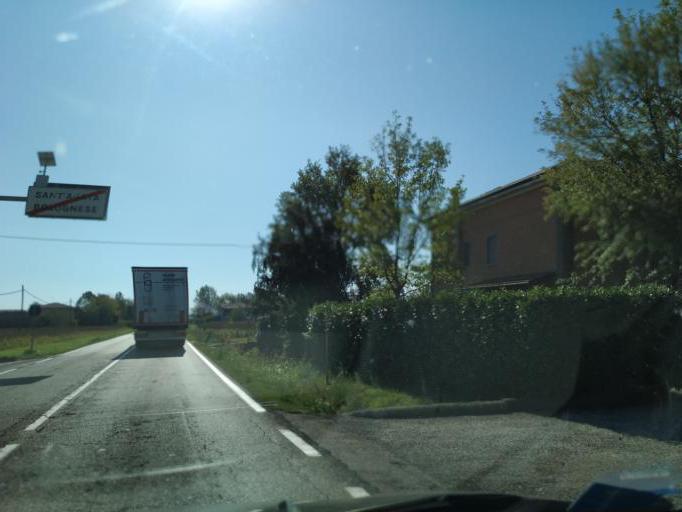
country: IT
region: Emilia-Romagna
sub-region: Provincia di Bologna
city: Sant'Agata Bolognese
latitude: 44.6558
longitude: 11.1382
